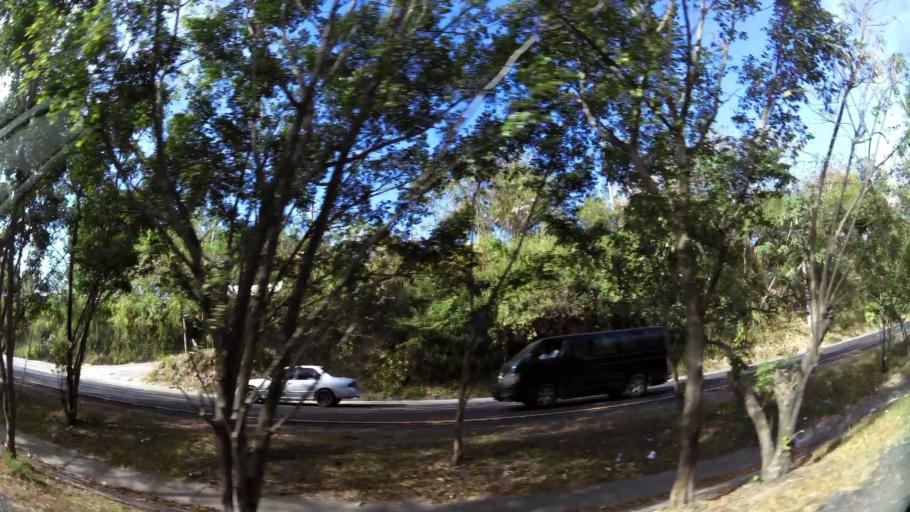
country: SV
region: Cuscatlan
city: Tecoluca
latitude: 13.7470
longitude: -89.0240
